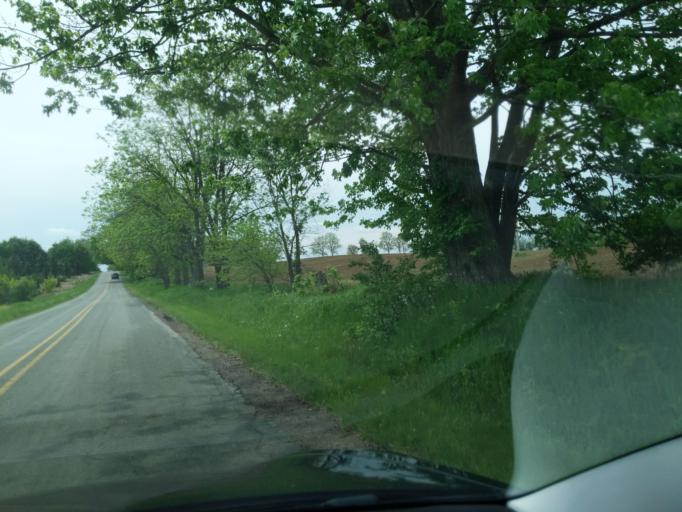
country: US
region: Michigan
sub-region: Ingham County
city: Stockbridge
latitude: 42.4247
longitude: -84.3029
